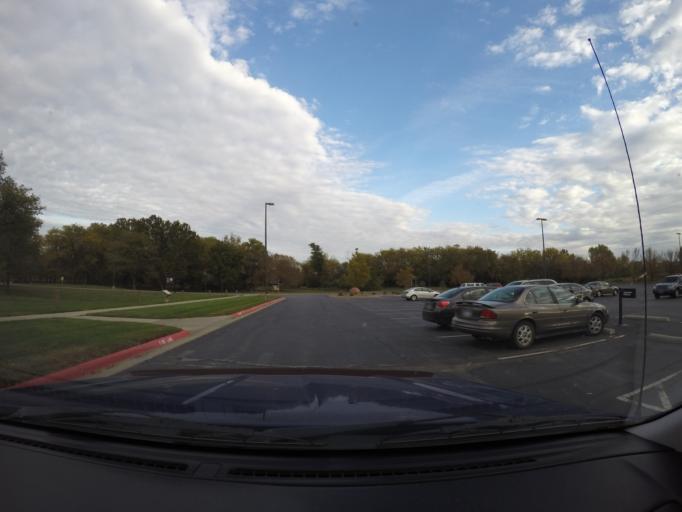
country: US
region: Kansas
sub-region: Shawnee County
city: Topeka
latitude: 39.0559
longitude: -95.7745
